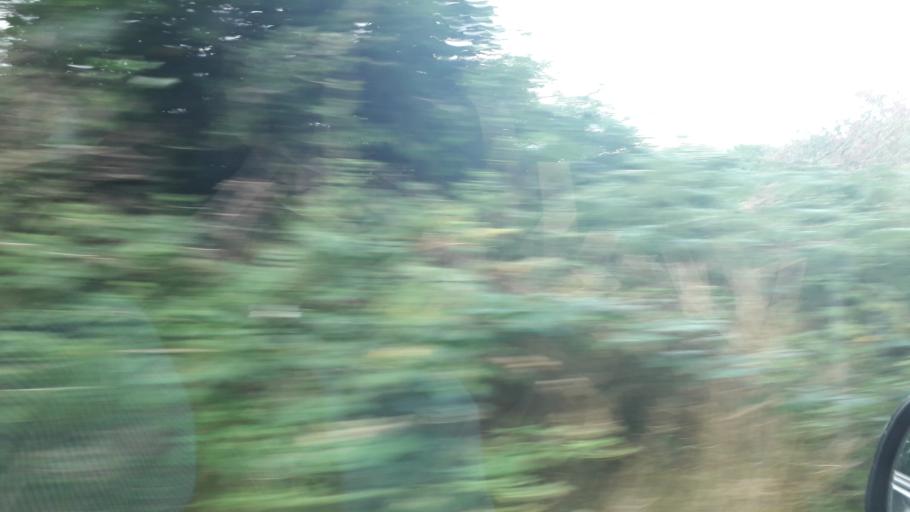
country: IE
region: Leinster
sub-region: Lu
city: Blackrock
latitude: 54.0412
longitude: -6.3324
